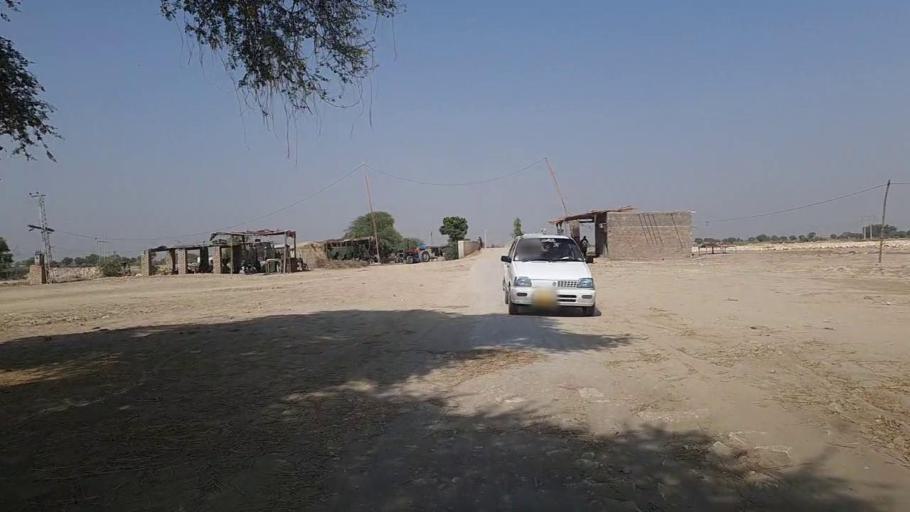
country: PK
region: Sindh
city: Kandhkot
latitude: 28.3886
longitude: 69.3271
